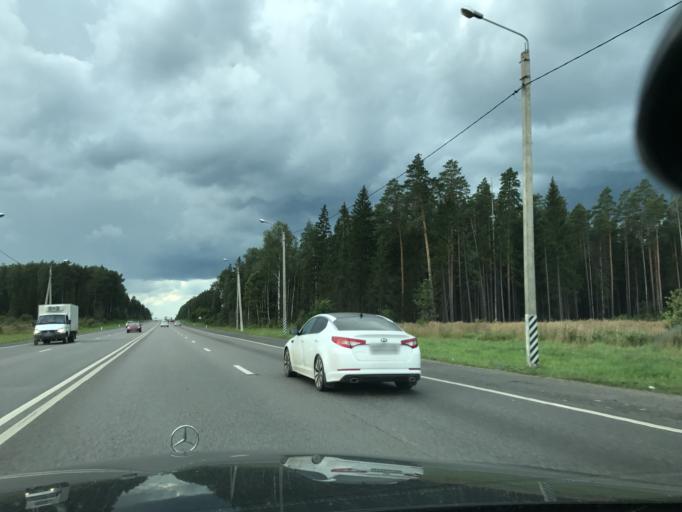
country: RU
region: Vladimir
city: Pokrov
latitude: 55.9274
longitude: 39.3114
